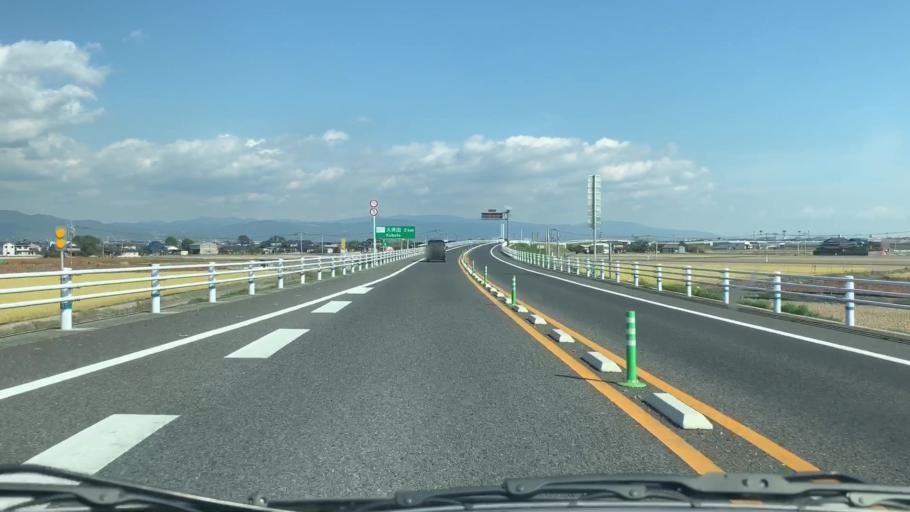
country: JP
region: Saga Prefecture
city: Saga-shi
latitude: 33.2246
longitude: 130.2168
